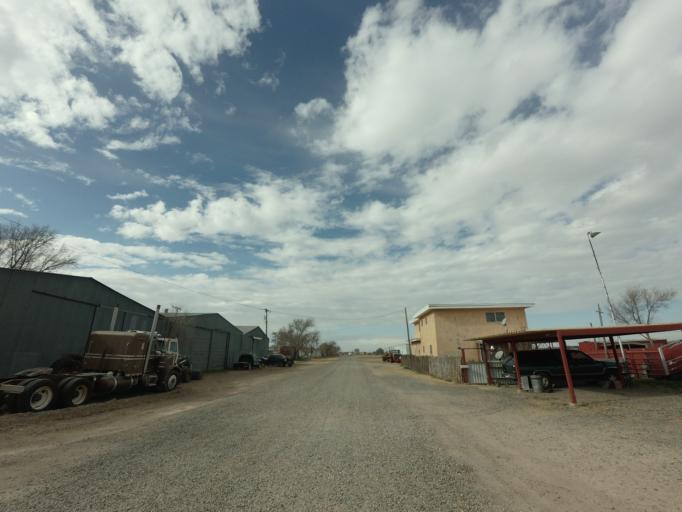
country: US
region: New Mexico
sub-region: Curry County
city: Clovis
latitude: 34.3939
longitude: -103.2168
